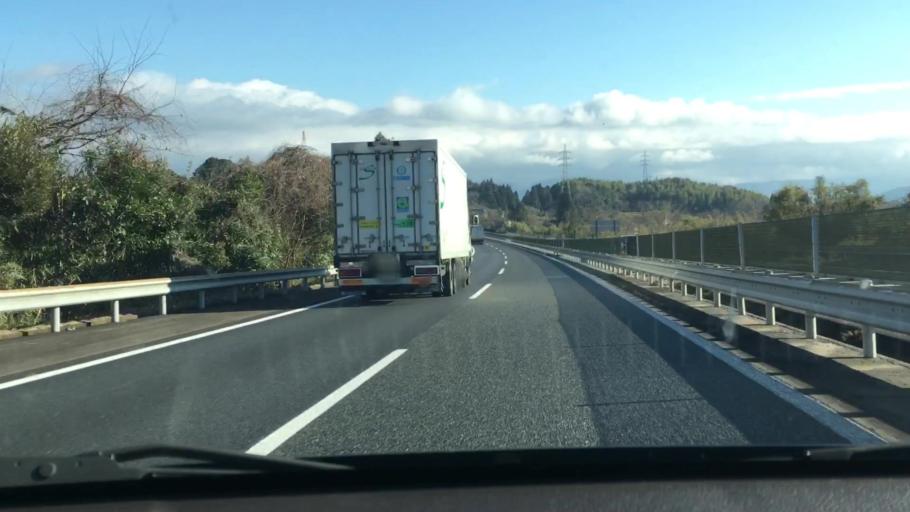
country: JP
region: Kumamoto
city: Hitoyoshi
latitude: 32.2373
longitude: 130.7625
